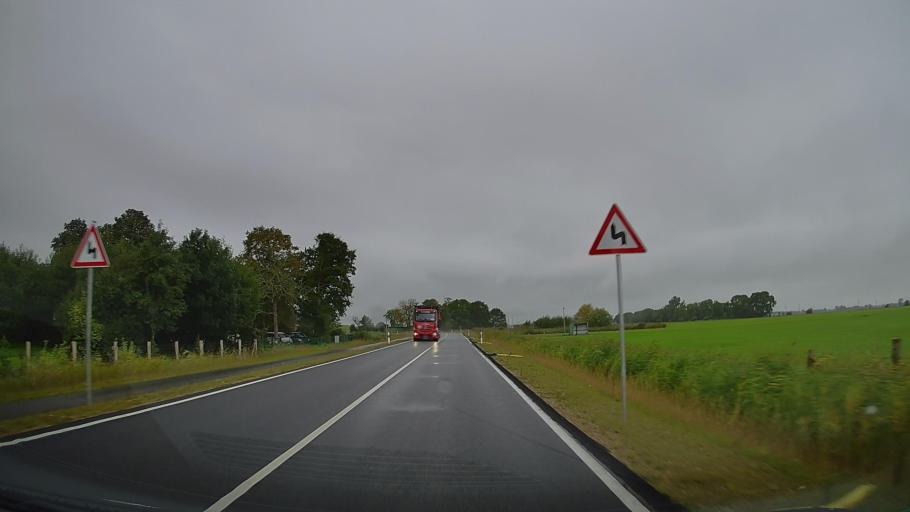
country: DE
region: Schleswig-Holstein
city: Brokdorf
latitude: 53.8717
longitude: 9.3009
